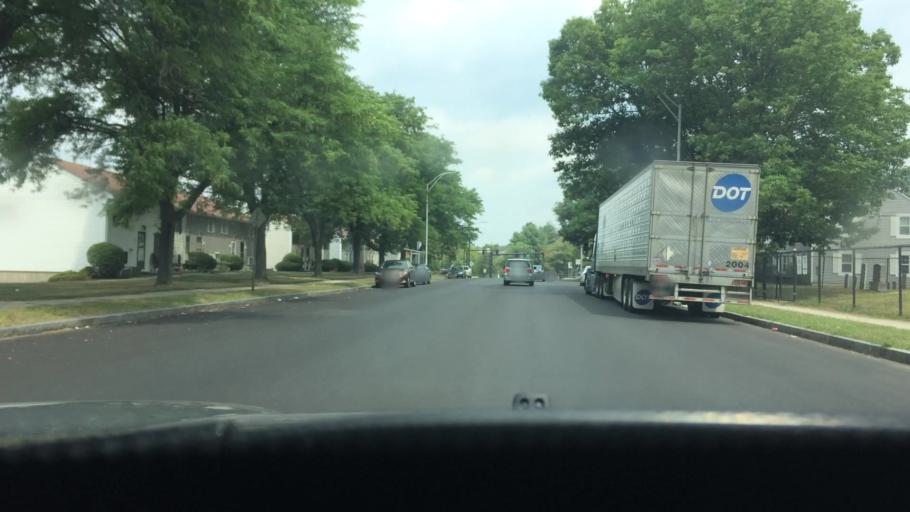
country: US
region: Massachusetts
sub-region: Hampden County
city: Chicopee
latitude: 42.1554
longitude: -72.5807
